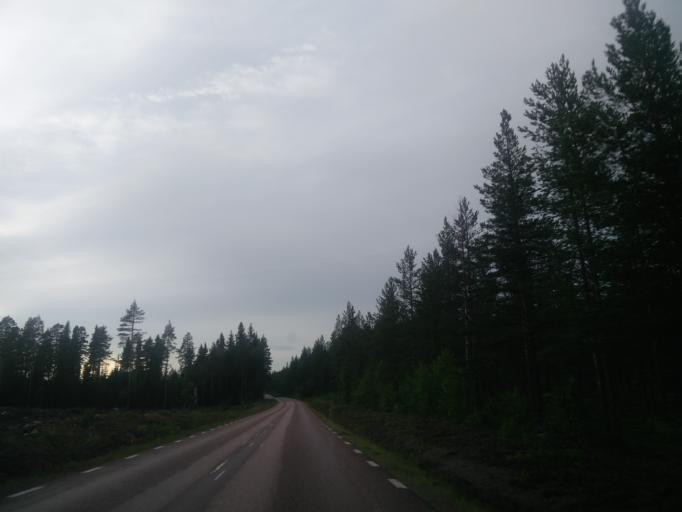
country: NO
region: Hedmark
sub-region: Trysil
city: Innbygda
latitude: 61.7786
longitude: 12.9423
